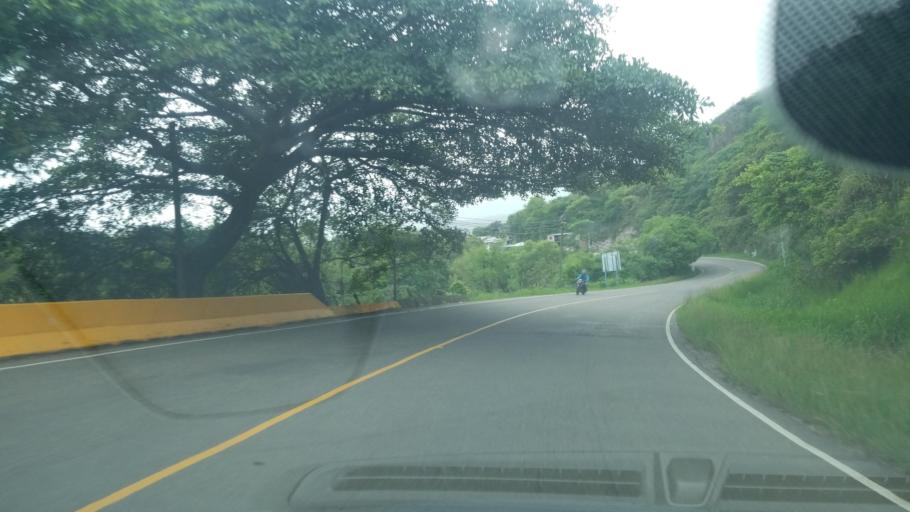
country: HN
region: Ocotepeque
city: Sinuapa
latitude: 14.4454
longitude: -89.1745
